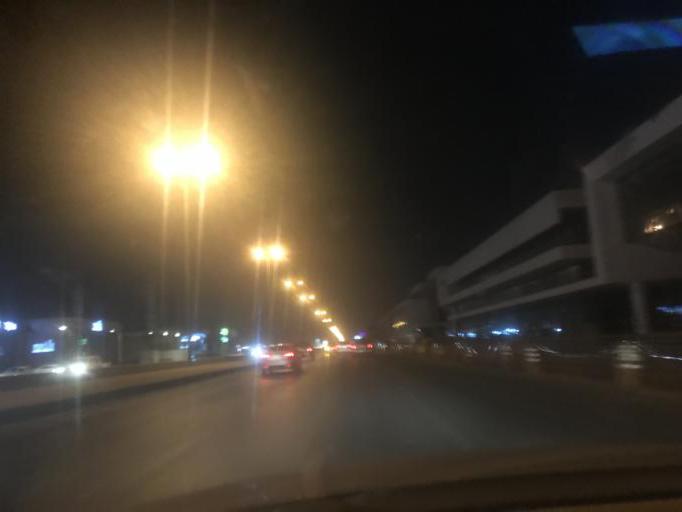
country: SA
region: Ar Riyad
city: Riyadh
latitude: 24.8336
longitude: 46.7344
